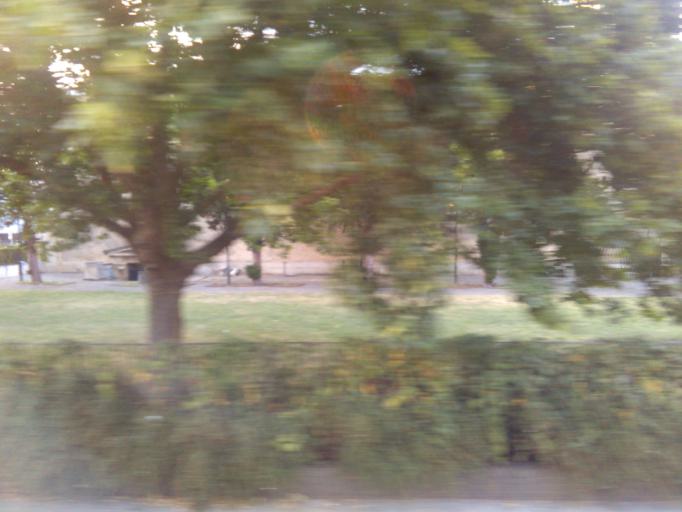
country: GB
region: England
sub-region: Greater London
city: Brixton Hill
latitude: 51.4593
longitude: -0.1160
